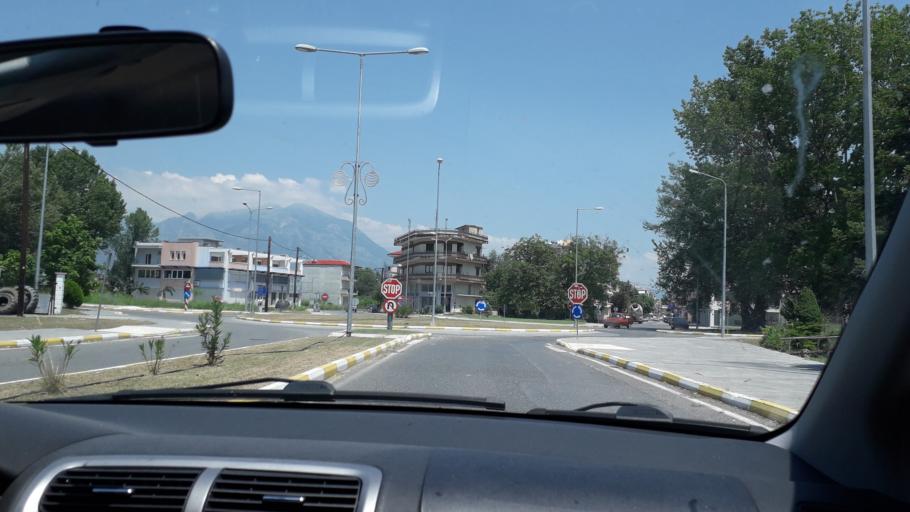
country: GR
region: Central Macedonia
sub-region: Nomos Pellis
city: Aridaia
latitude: 40.9705
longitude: 22.0568
